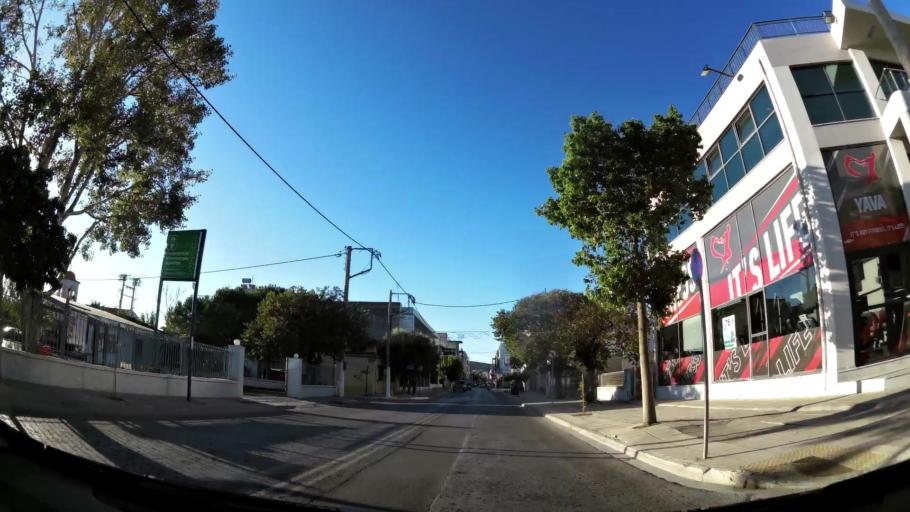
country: GR
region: Attica
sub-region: Nomarchia Anatolikis Attikis
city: Koropi
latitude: 37.9097
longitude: 23.8735
